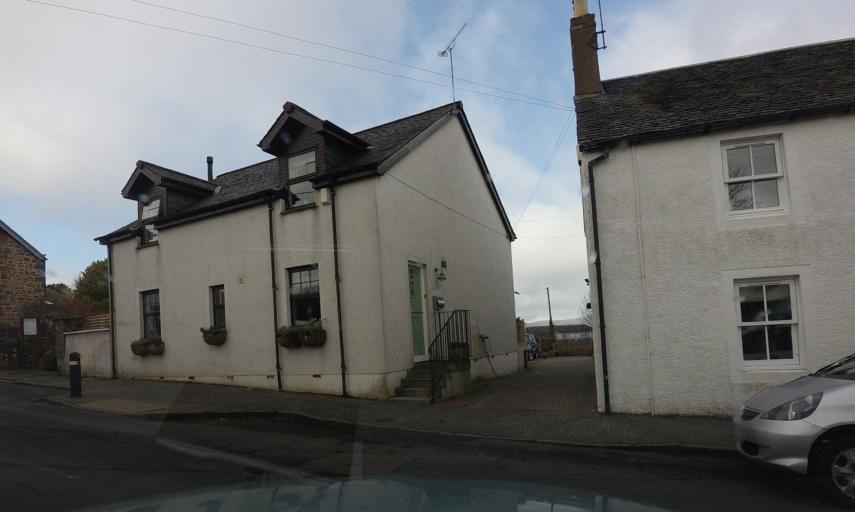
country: GB
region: Scotland
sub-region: Stirling
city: Callander
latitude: 56.1260
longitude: -4.1725
